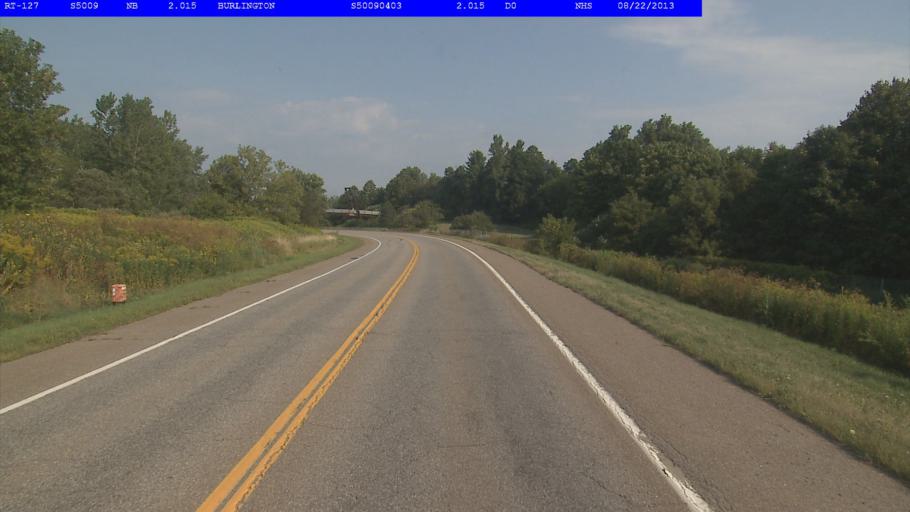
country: US
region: Vermont
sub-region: Chittenden County
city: Burlington
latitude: 44.5132
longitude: -73.2348
